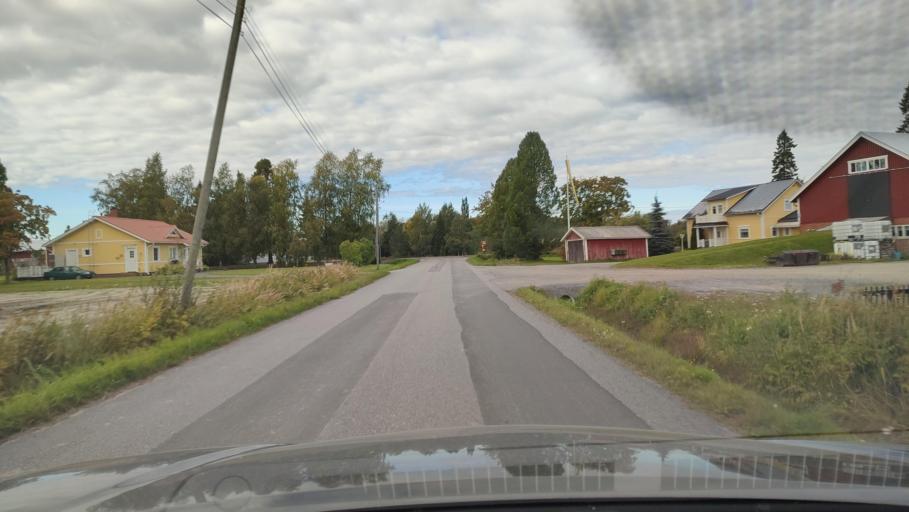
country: FI
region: Southern Ostrobothnia
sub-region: Suupohja
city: Karijoki
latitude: 62.2374
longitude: 21.5782
